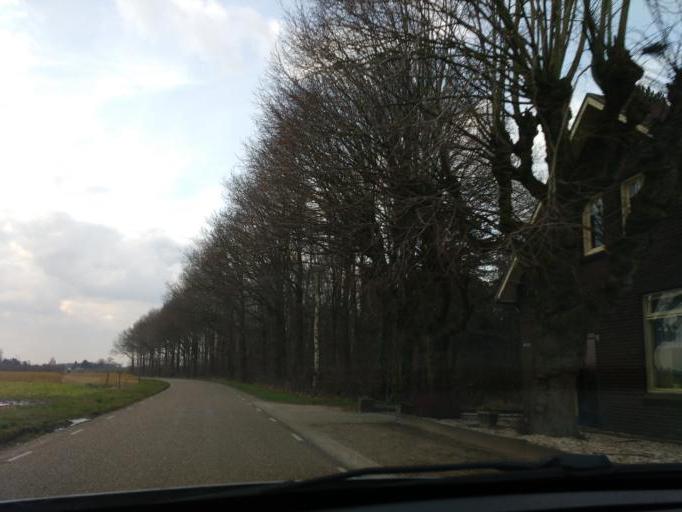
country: NL
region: Limburg
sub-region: Gemeente Venray
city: Venray
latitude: 51.5725
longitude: 6.0206
